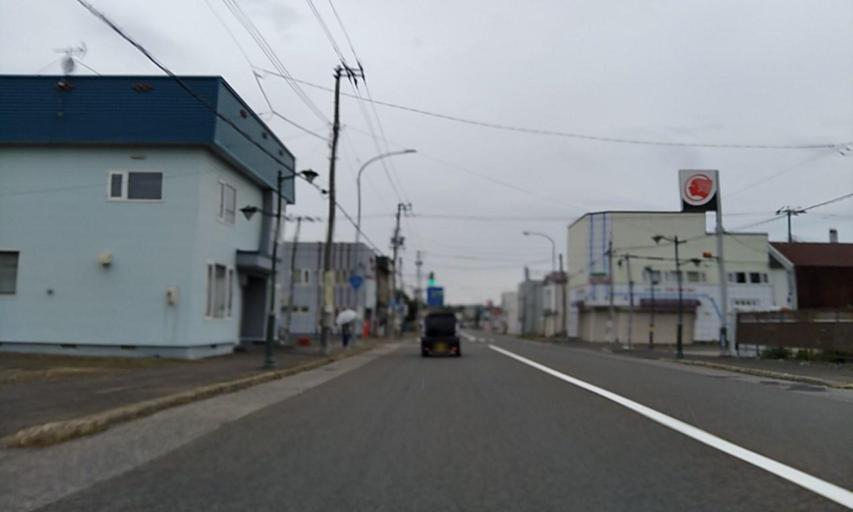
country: JP
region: Hokkaido
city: Bihoro
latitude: 43.9143
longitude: 144.1740
